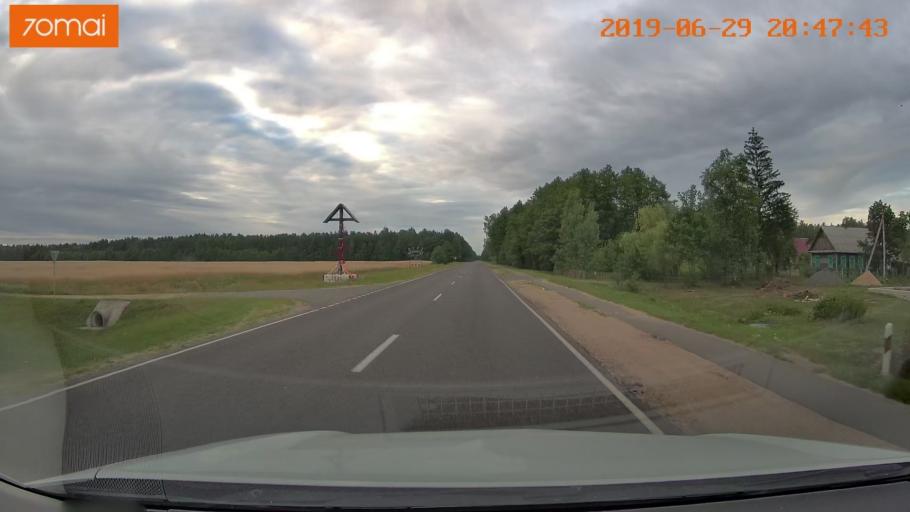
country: BY
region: Brest
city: Hantsavichy
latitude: 52.6415
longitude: 26.3161
